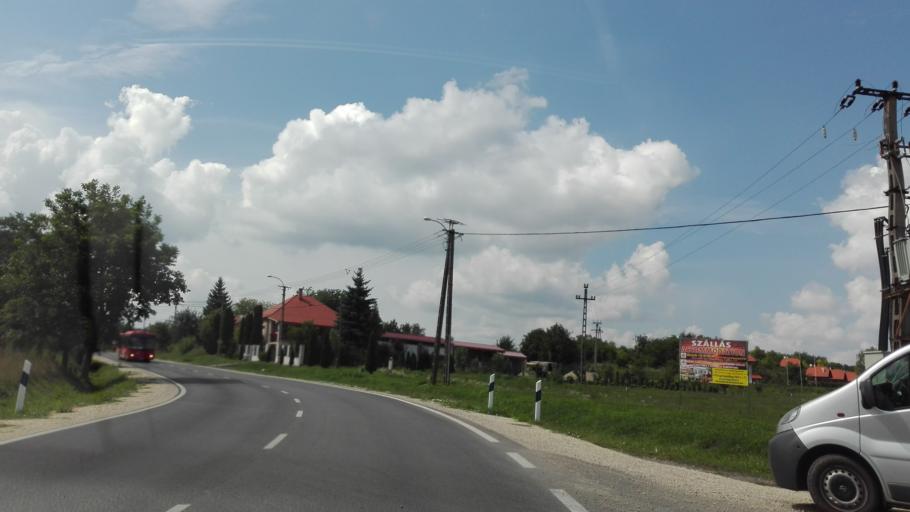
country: HU
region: Tolna
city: Simontornya
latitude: 46.7603
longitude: 18.5403
